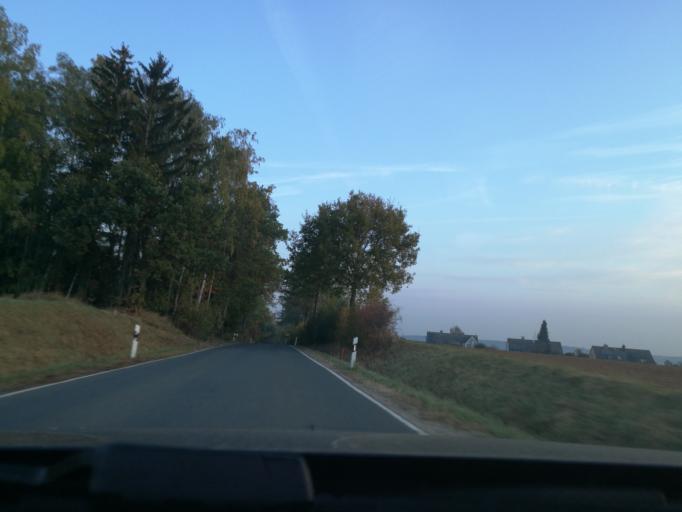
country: DE
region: Bavaria
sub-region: Regierungsbezirk Mittelfranken
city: Obermichelbach
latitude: 49.5515
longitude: 10.9145
